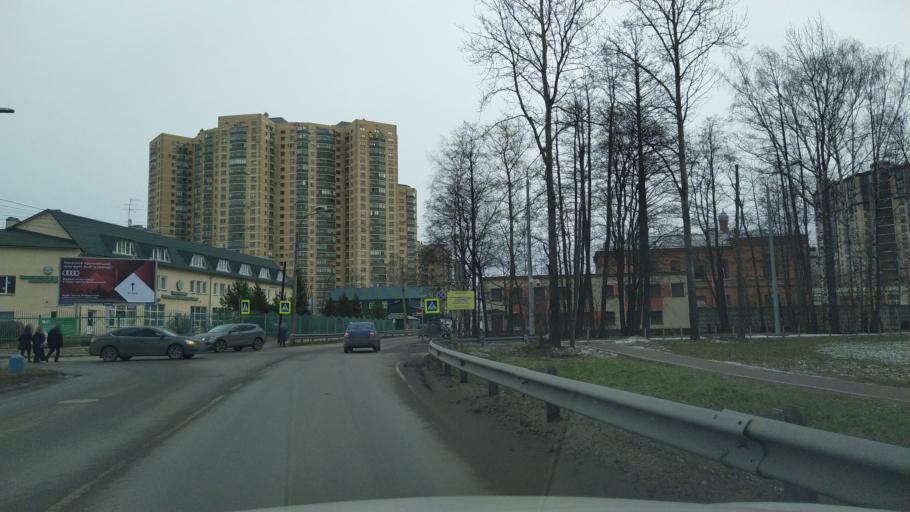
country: RU
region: Leningrad
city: Udel'naya
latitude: 60.0156
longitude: 30.3047
